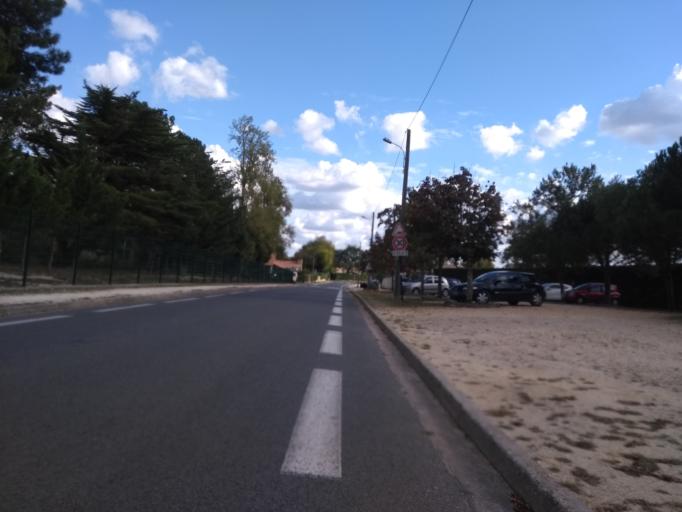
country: FR
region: Aquitaine
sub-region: Departement de la Gironde
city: Gradignan
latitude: 44.7813
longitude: -0.5979
